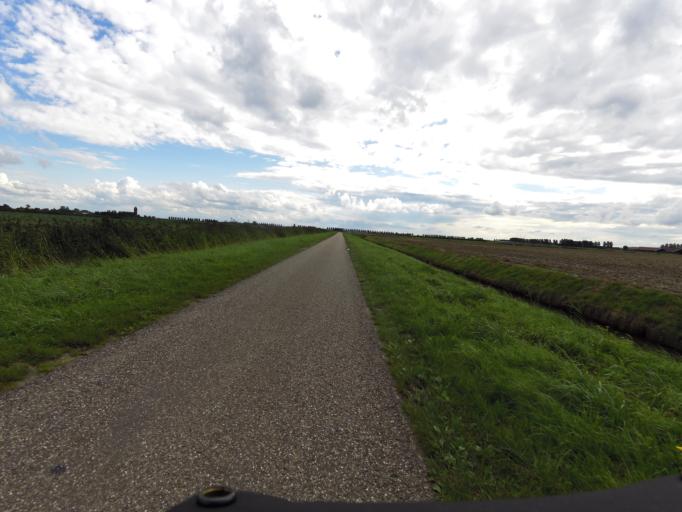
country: NL
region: South Holland
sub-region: Gemeente Goeree-Overflakkee
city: Middelharnis
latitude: 51.7117
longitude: 4.2431
